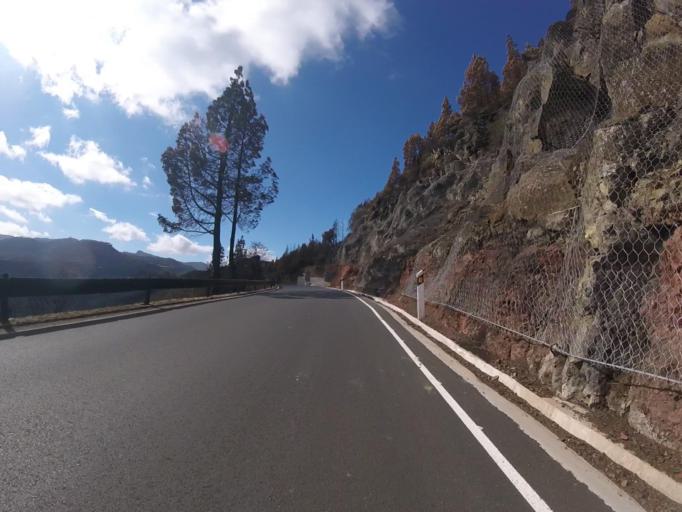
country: ES
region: Canary Islands
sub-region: Provincia de Las Palmas
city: Tejeda
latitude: 27.9992
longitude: -15.5952
